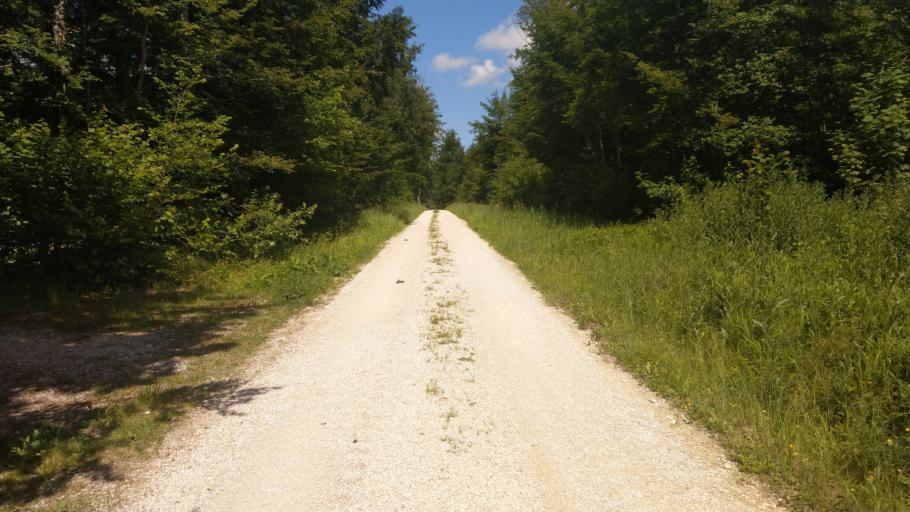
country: DE
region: Baden-Wuerttemberg
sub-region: Regierungsbezirk Stuttgart
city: Bartholoma
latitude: 48.7494
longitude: 10.0357
